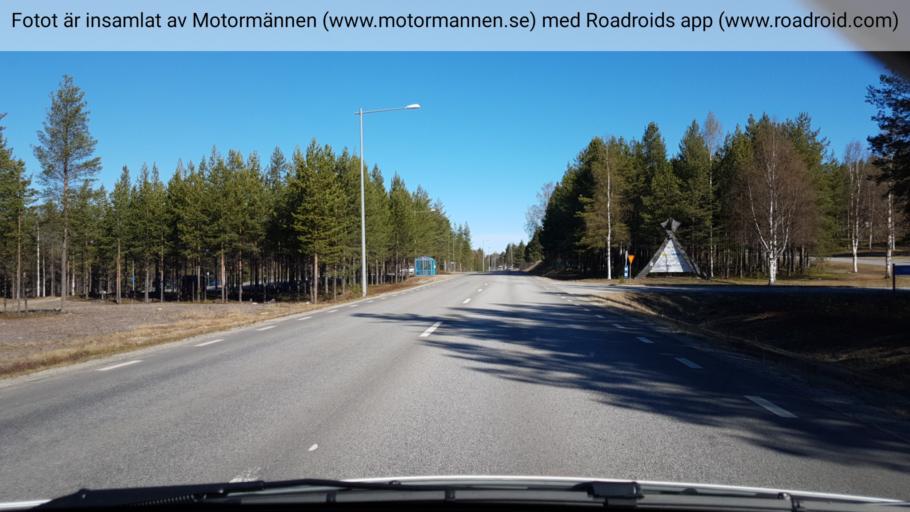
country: SE
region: Vaesterbotten
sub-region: Lycksele Kommun
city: Lycksele
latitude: 64.5750
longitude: 18.7103
